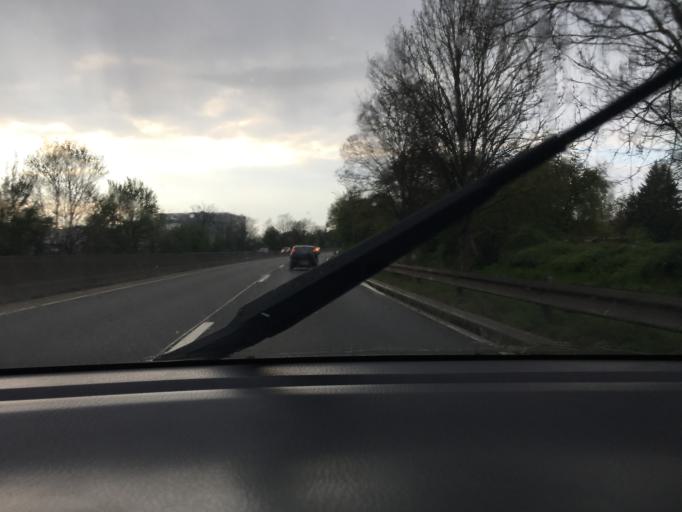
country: DE
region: Rheinland-Pfalz
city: Sankt Sebastian
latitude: 50.4183
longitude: 7.5708
